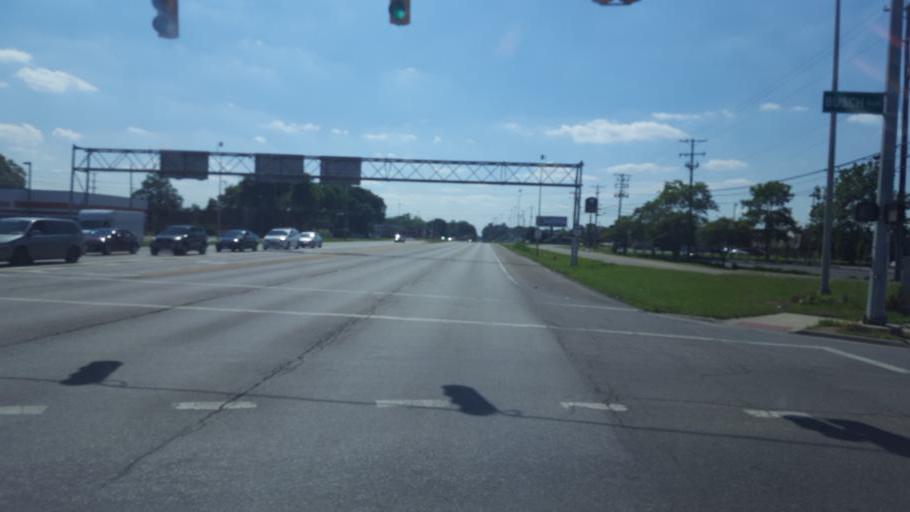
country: US
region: Ohio
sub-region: Franklin County
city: Worthington
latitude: 40.0879
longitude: -82.9928
